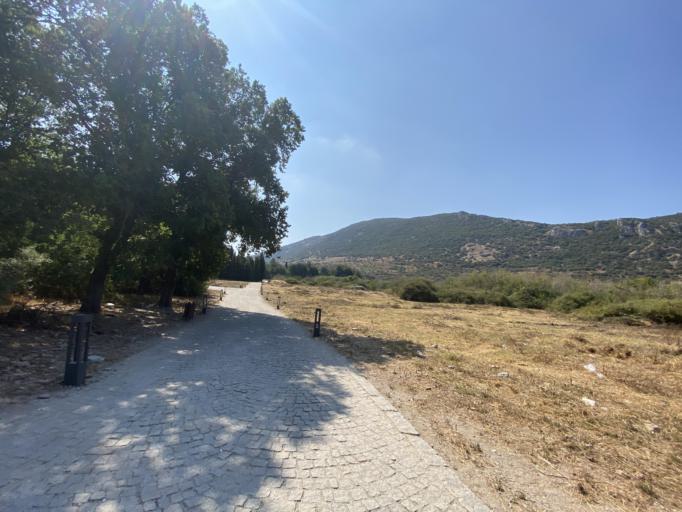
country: TR
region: Izmir
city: Selcuk
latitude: 37.9439
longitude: 27.3403
